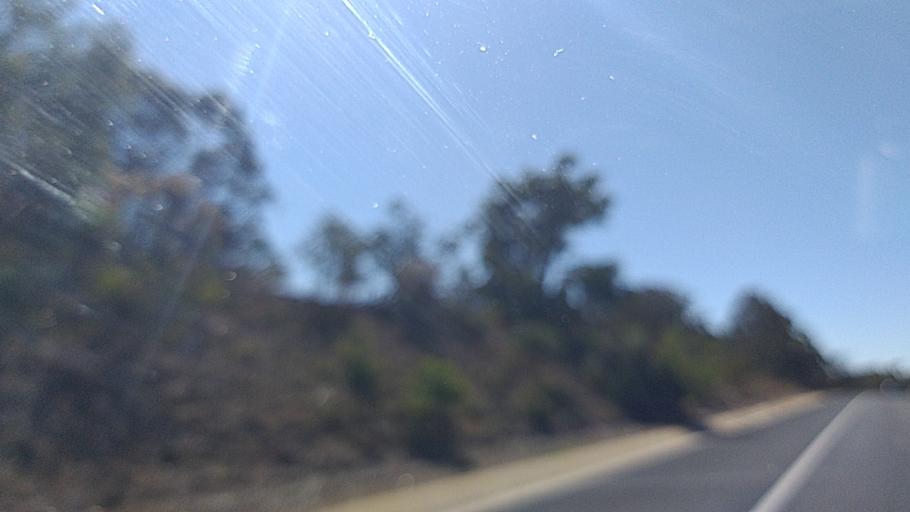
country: AU
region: Australian Capital Territory
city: Kaleen
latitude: -35.1846
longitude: 149.2306
